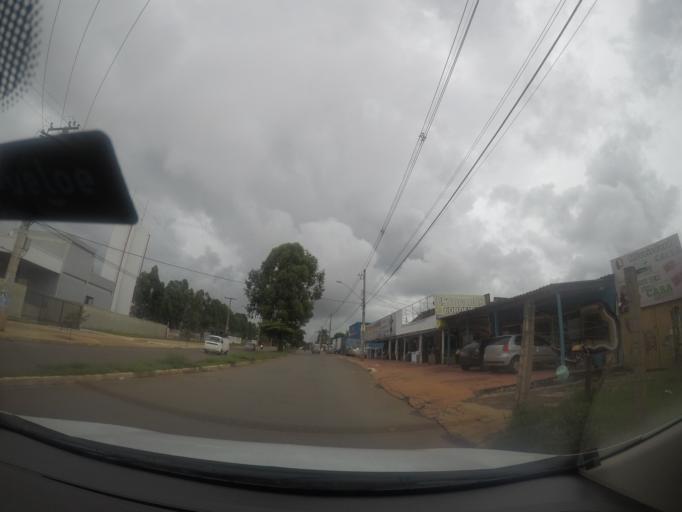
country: BR
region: Goias
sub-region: Trindade
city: Trindade
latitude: -16.6529
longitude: -49.3845
